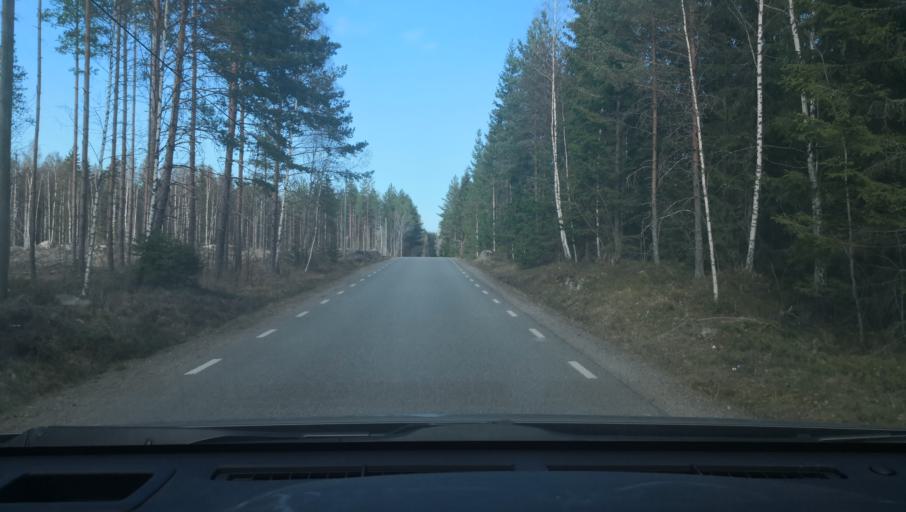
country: SE
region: Uppsala
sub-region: Heby Kommun
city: Heby
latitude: 59.9177
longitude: 16.8392
